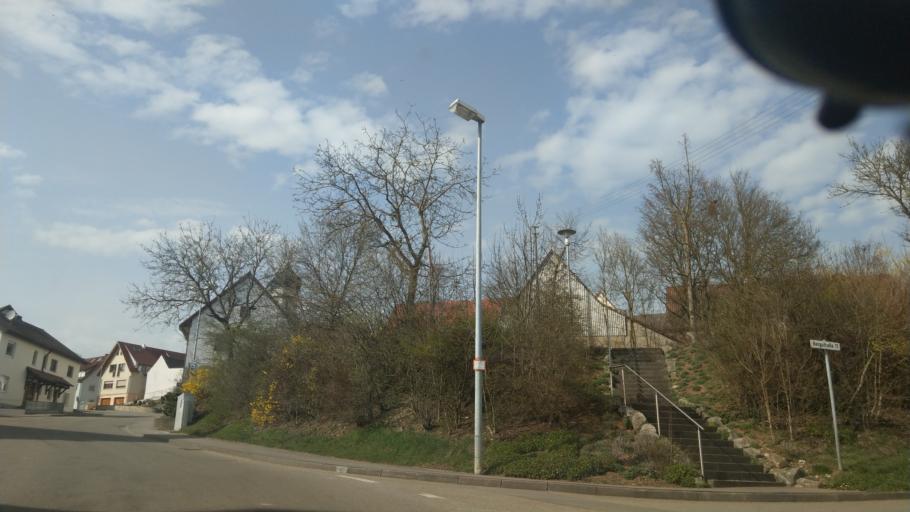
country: DE
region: Baden-Wuerttemberg
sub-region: Tuebingen Region
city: Ollingen
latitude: 48.5281
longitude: 10.1482
